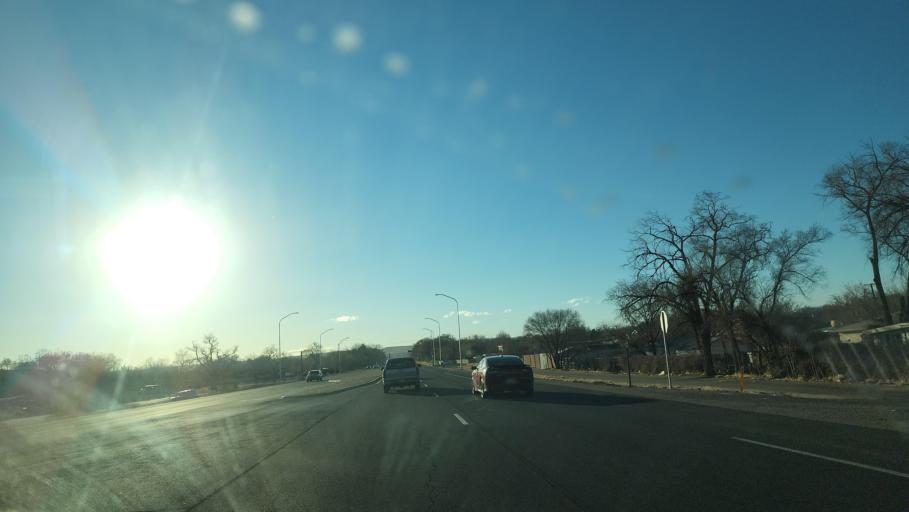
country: US
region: New Mexico
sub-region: Bernalillo County
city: South Valley
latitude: 35.0269
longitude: -106.6873
